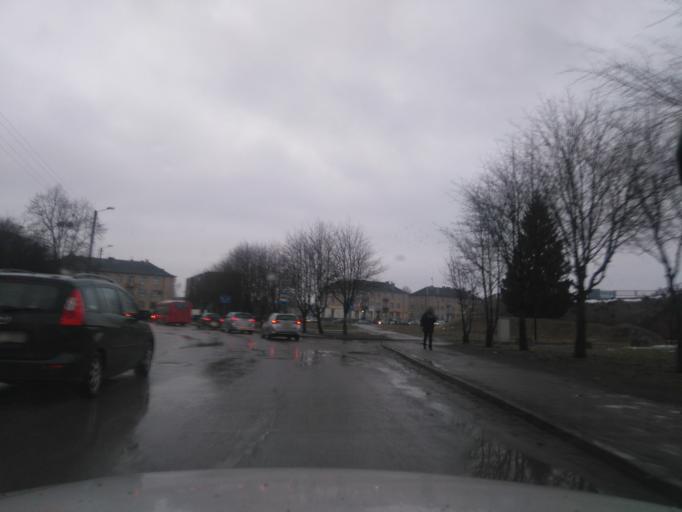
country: LT
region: Kauno apskritis
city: Dainava (Kaunas)
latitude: 54.8965
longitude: 23.9565
